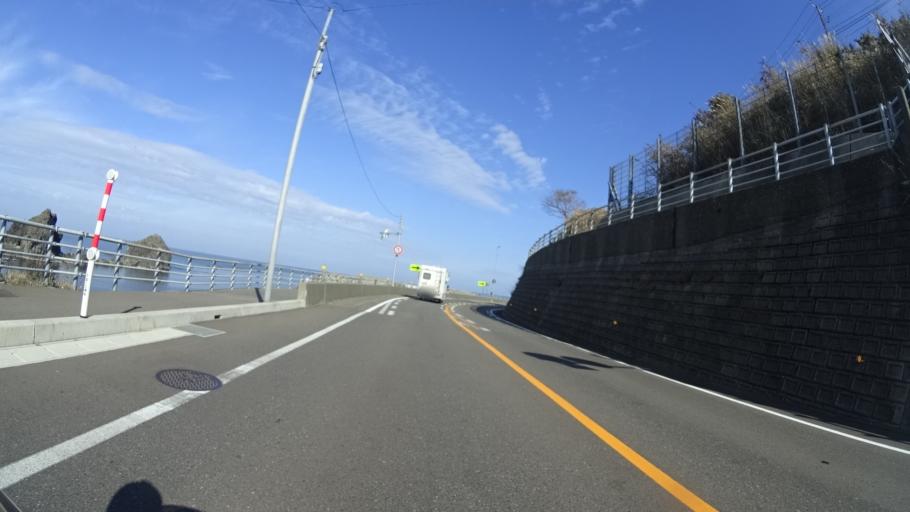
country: JP
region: Niigata
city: Itoigawa
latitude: 37.1083
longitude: 137.9939
